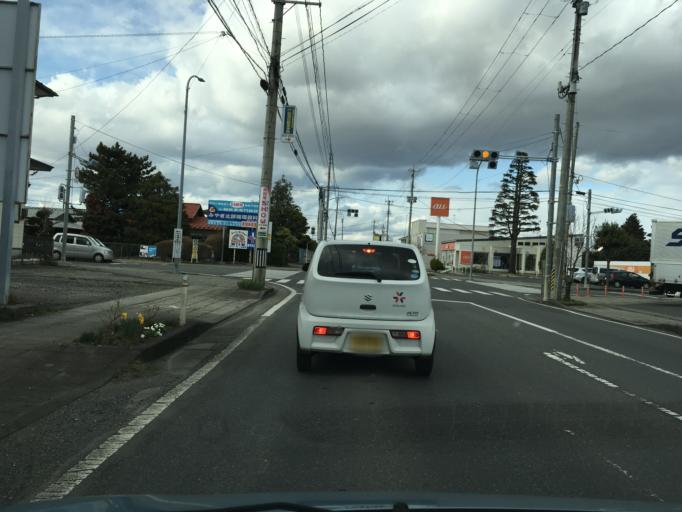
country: JP
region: Miyagi
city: Wakuya
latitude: 38.6797
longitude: 141.1948
